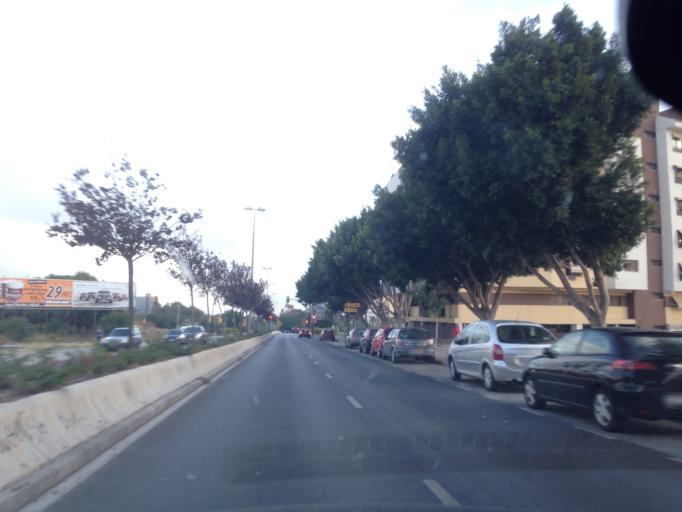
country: ES
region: Andalusia
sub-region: Provincia de Malaga
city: Malaga
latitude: 36.7282
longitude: -4.4647
